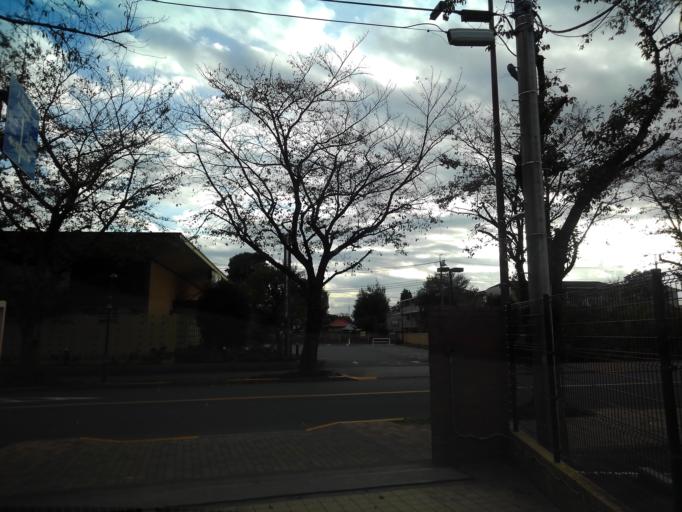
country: JP
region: Tokyo
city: Mitaka-shi
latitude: 35.6808
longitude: 139.5765
